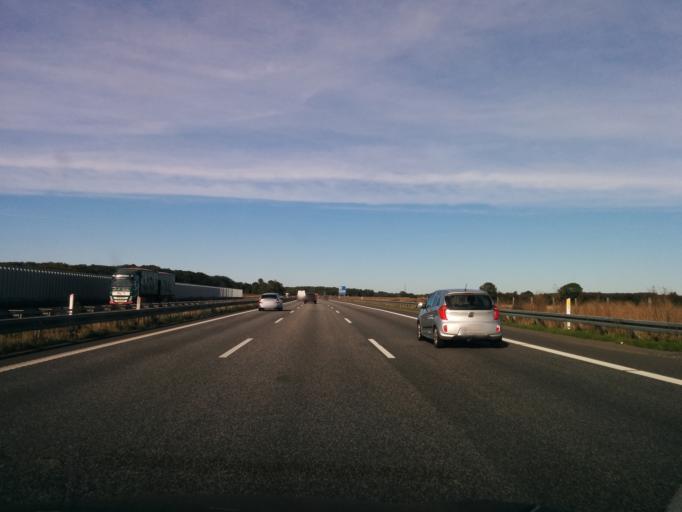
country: DK
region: South Denmark
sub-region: Vejle Kommune
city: Borkop
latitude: 55.6206
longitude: 9.5748
